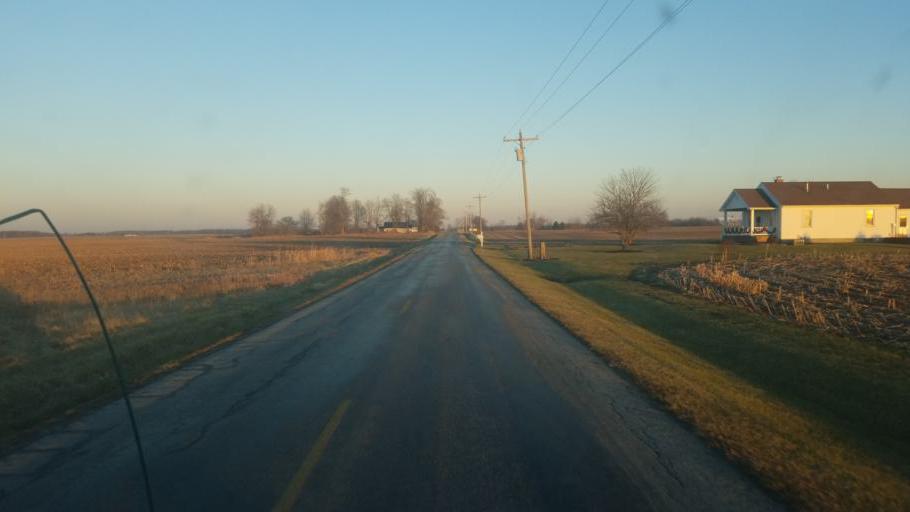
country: US
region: Ohio
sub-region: Union County
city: Richwood
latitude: 40.6220
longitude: -83.3533
